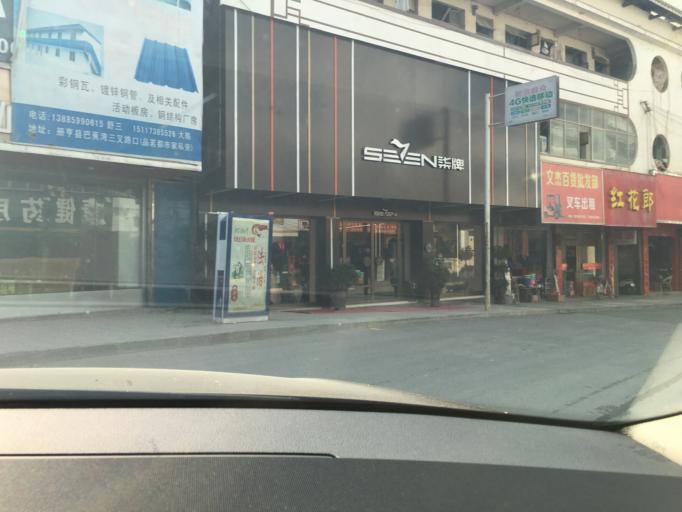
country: CN
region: Guangxi Zhuangzu Zizhiqu
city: Xinzhou
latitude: 24.9846
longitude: 105.8048
